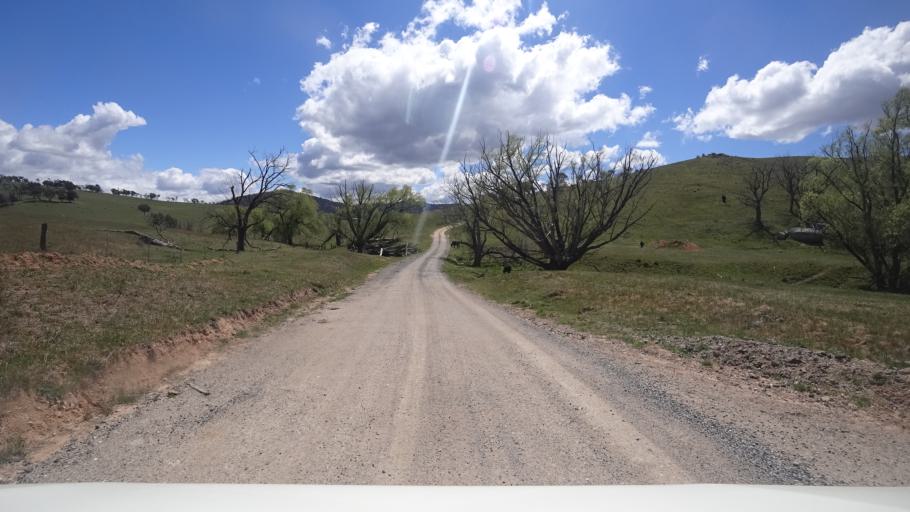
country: AU
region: New South Wales
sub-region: Oberon
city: Oberon
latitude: -33.5762
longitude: 149.9416
